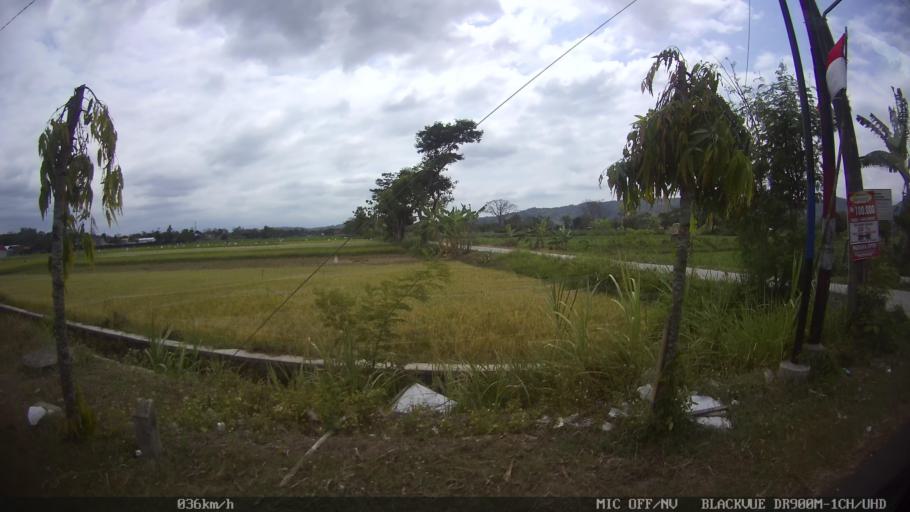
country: ID
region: Central Java
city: Candi Prambanan
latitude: -7.8102
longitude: 110.4843
